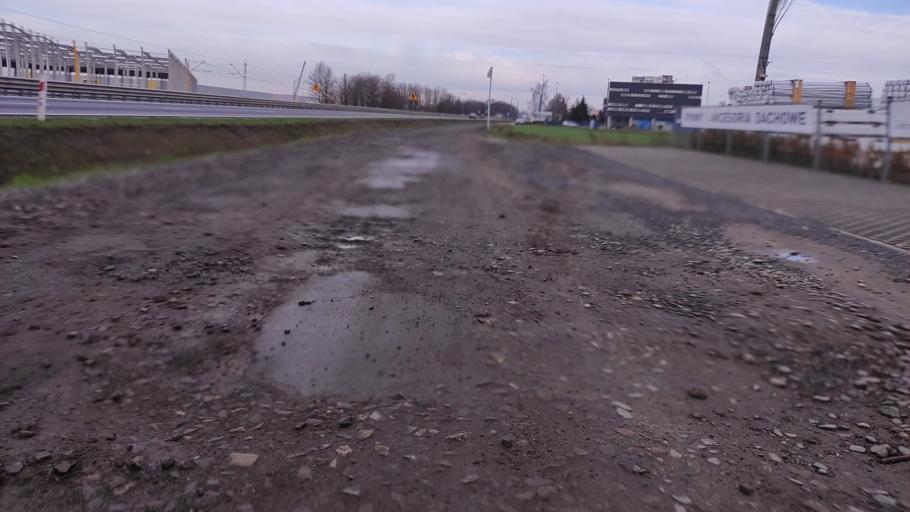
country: PL
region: Greater Poland Voivodeship
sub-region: Powiat poznanski
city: Swarzedz
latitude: 52.3989
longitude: 17.1432
